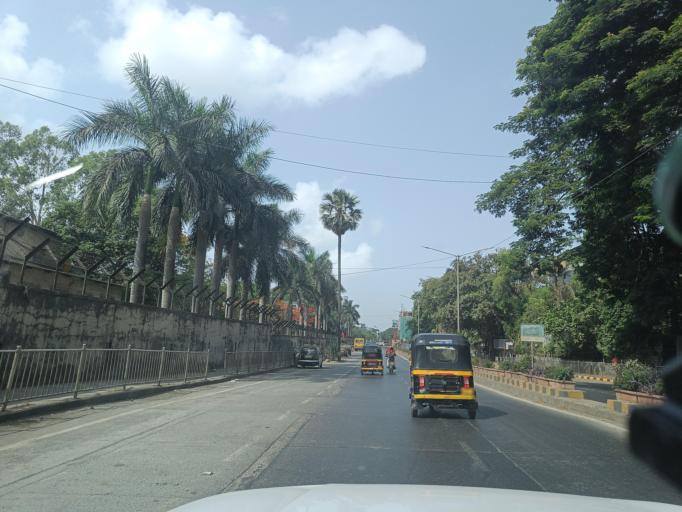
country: IN
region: Maharashtra
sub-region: Mumbai Suburban
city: Powai
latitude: 19.1285
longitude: 72.8754
